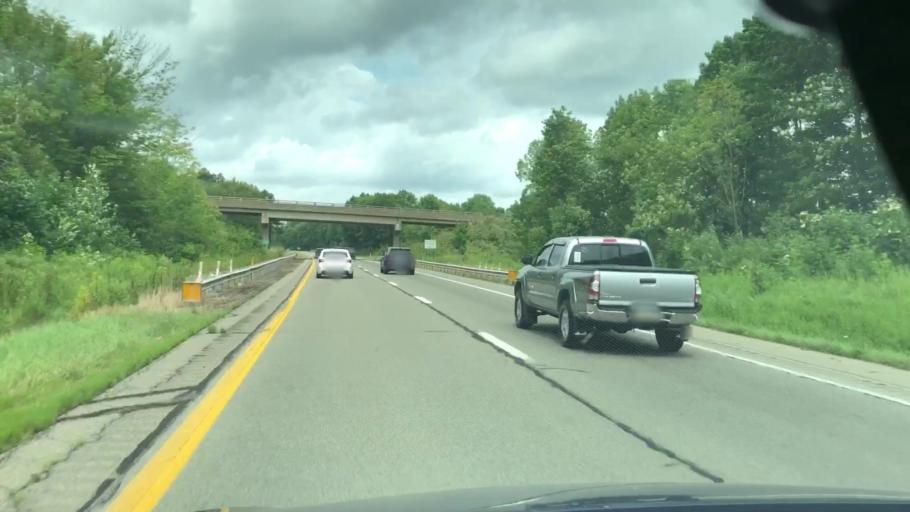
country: US
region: Pennsylvania
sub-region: Erie County
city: Edinboro
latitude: 41.7915
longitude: -80.1759
